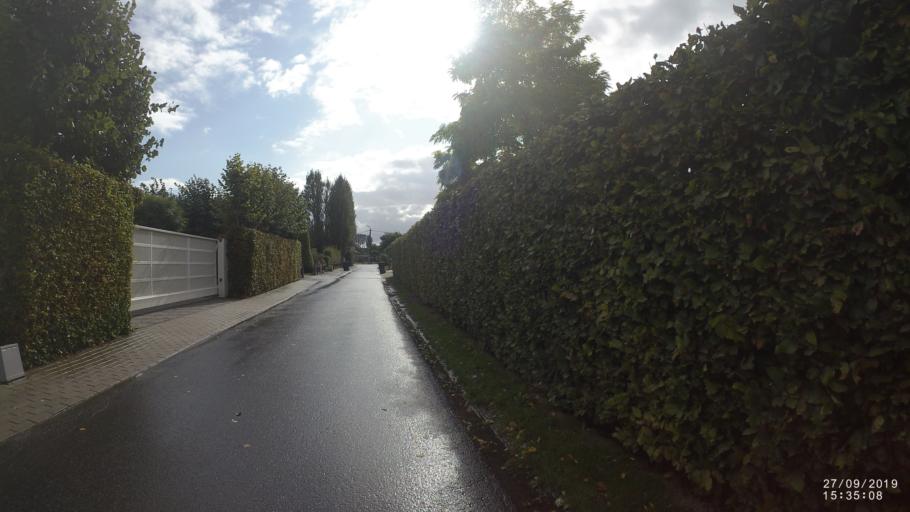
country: BE
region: Flanders
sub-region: Provincie Oost-Vlaanderen
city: Zottegem
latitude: 50.8770
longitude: 3.7408
